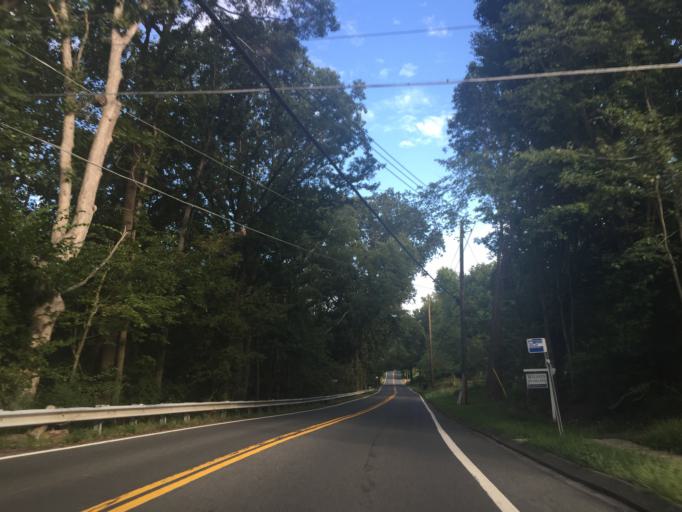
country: US
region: Maryland
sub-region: Montgomery County
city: Montgomery Village
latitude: 39.2045
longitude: -77.1633
